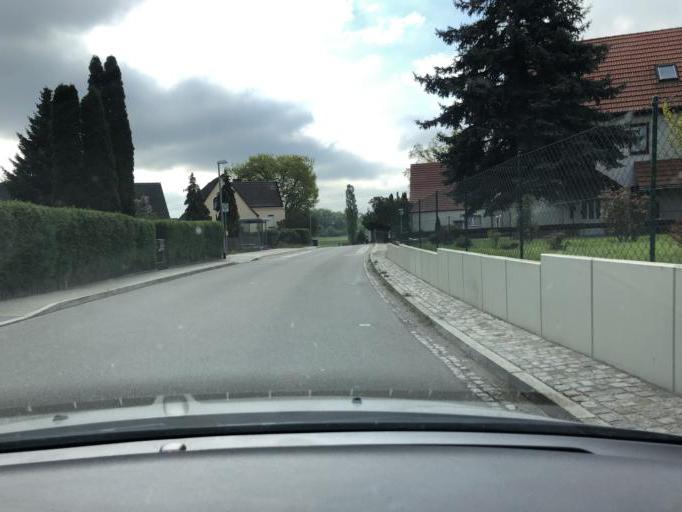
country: DE
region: Thuringia
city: Haselbach
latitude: 51.0544
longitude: 12.4398
